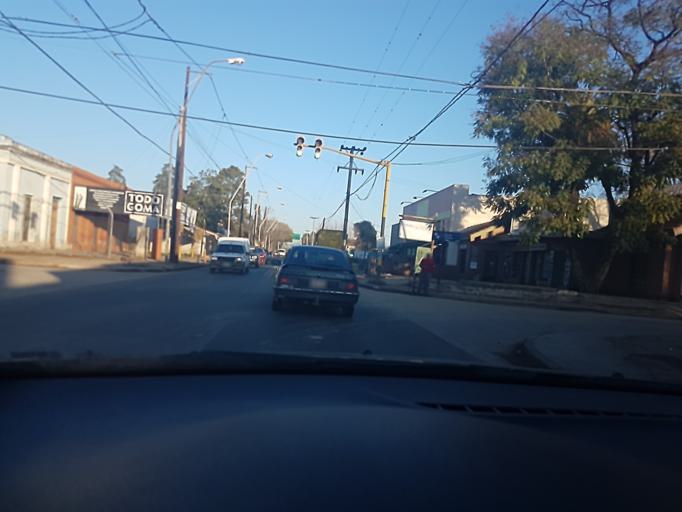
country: AR
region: Cordoba
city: Villa Allende
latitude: -31.3433
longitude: -64.2326
